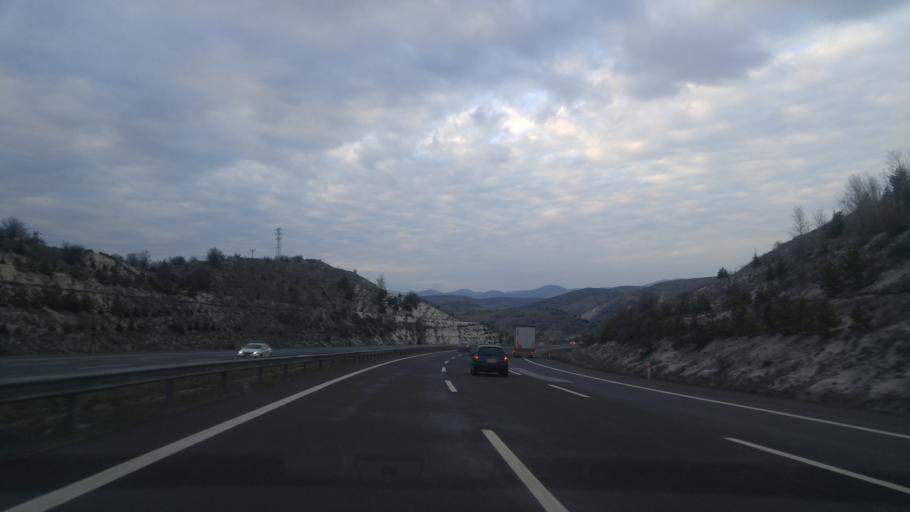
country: TR
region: Ankara
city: Celtikci
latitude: 40.3992
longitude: 32.4392
